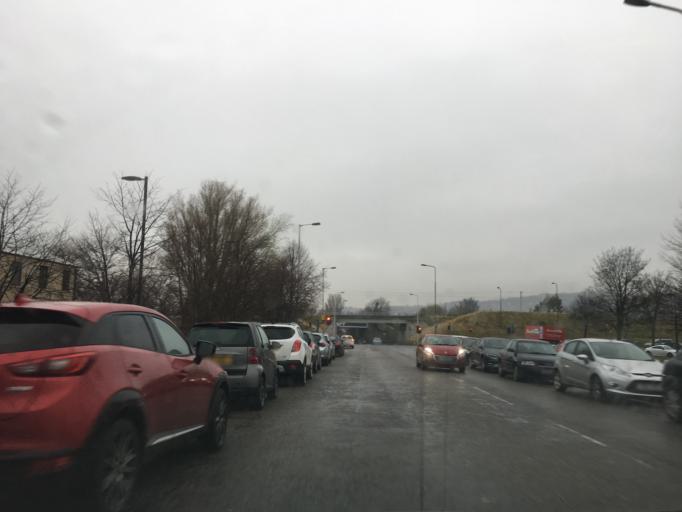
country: GB
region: Scotland
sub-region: Edinburgh
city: Colinton
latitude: 55.9311
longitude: -3.2735
